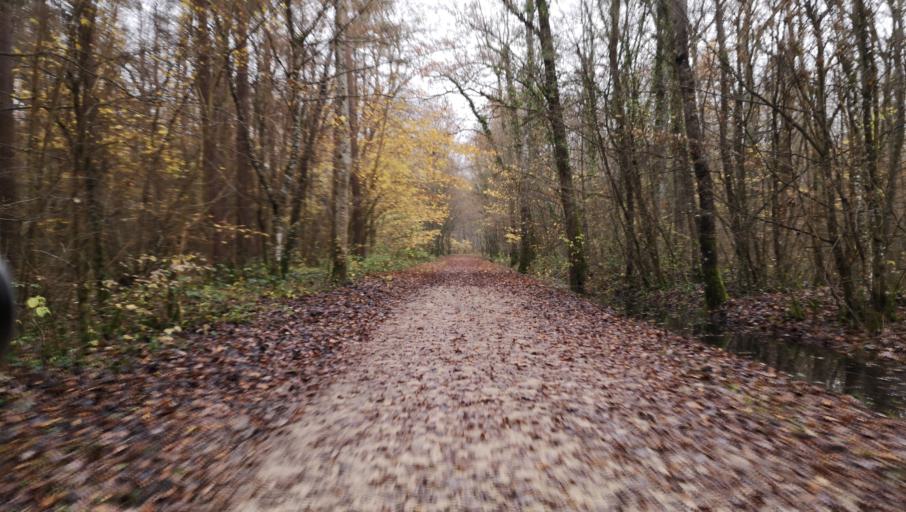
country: FR
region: Centre
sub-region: Departement du Loiret
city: Boigny-sur-Bionne
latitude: 47.9422
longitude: 1.9964
